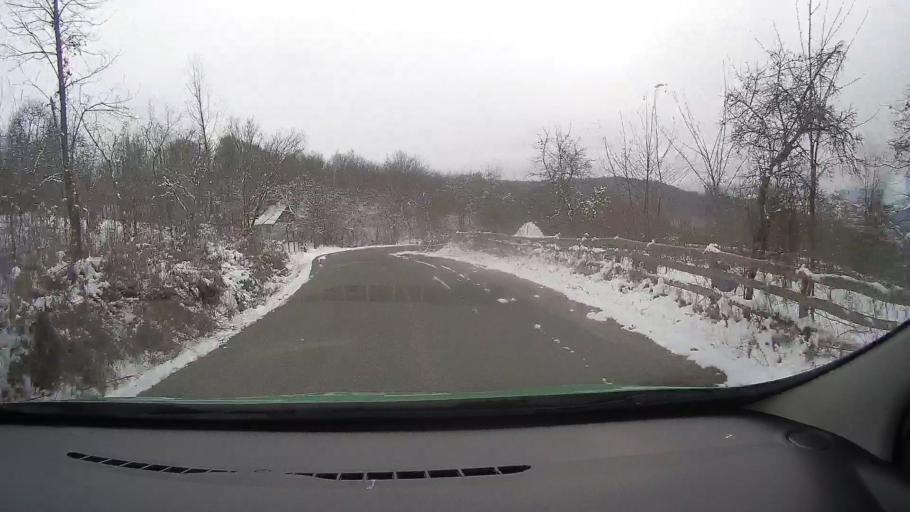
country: RO
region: Alba
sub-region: Comuna Almasu Mare
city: Almasu Mare
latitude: 46.0847
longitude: 23.1297
